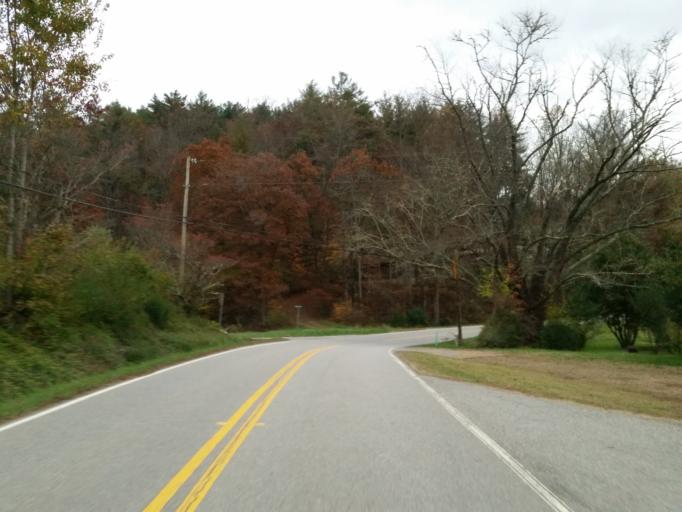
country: US
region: Georgia
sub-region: Union County
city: Blairsville
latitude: 34.7146
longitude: -84.0641
